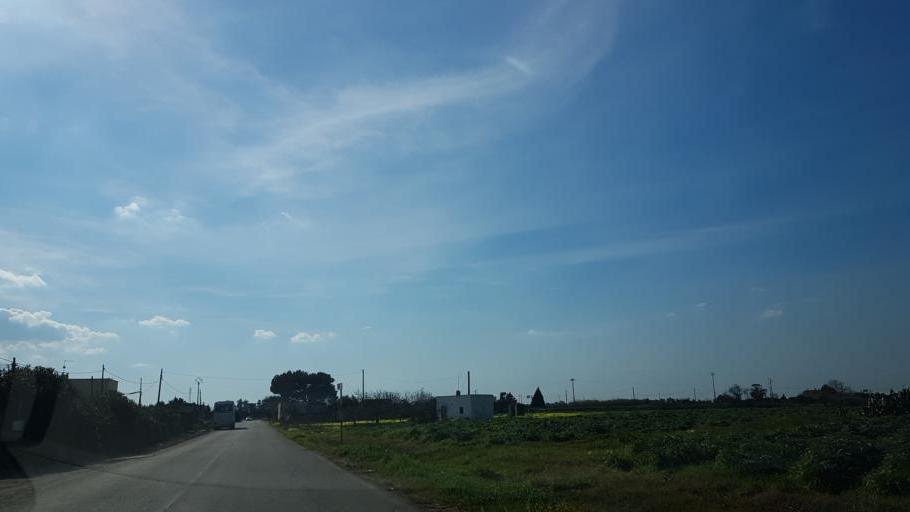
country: IT
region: Apulia
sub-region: Provincia di Brindisi
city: San Vito dei Normanni
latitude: 40.6926
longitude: 17.8257
